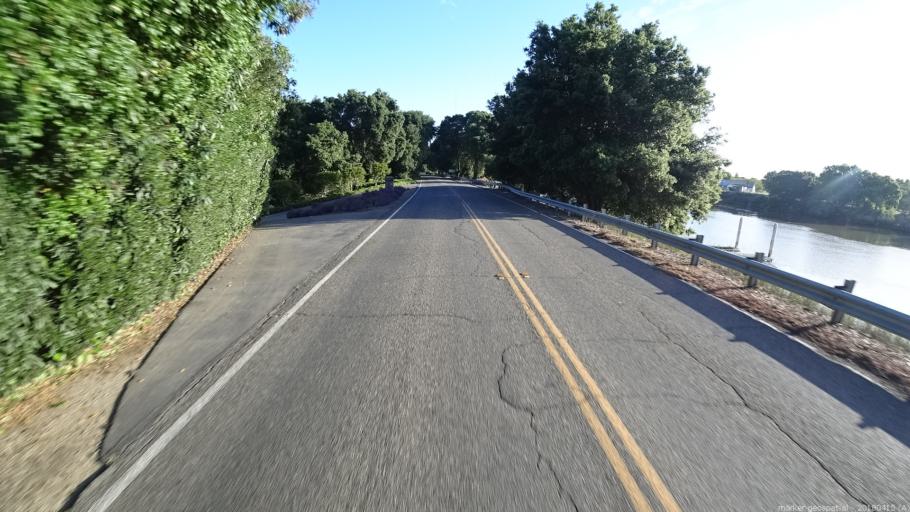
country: US
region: California
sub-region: Sacramento County
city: Walnut Grove
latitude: 38.2475
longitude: -121.5117
